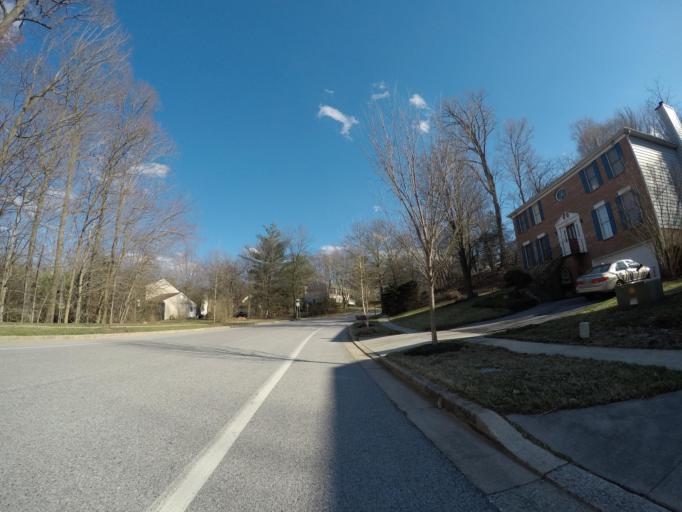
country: US
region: Maryland
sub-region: Howard County
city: Ellicott City
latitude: 39.2580
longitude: -76.8081
